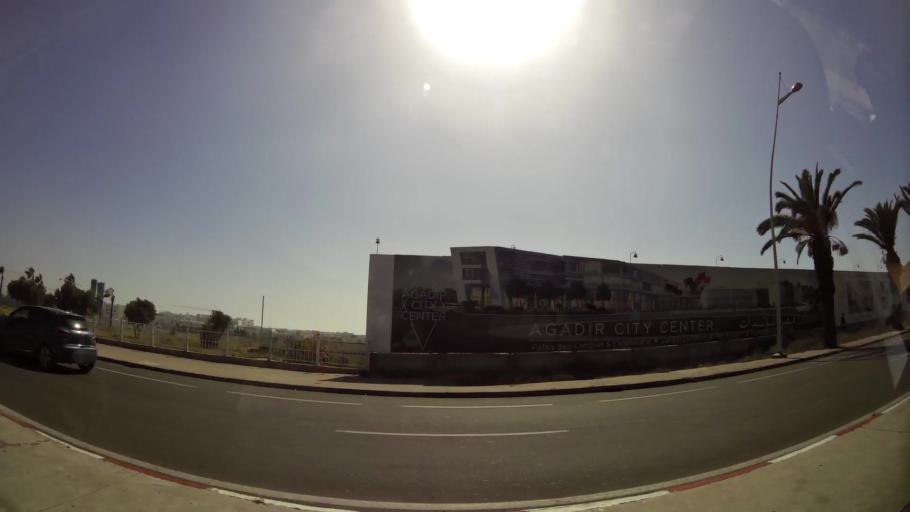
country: MA
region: Souss-Massa-Draa
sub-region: Agadir-Ida-ou-Tnan
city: Agadir
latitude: 30.4065
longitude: -9.5875
